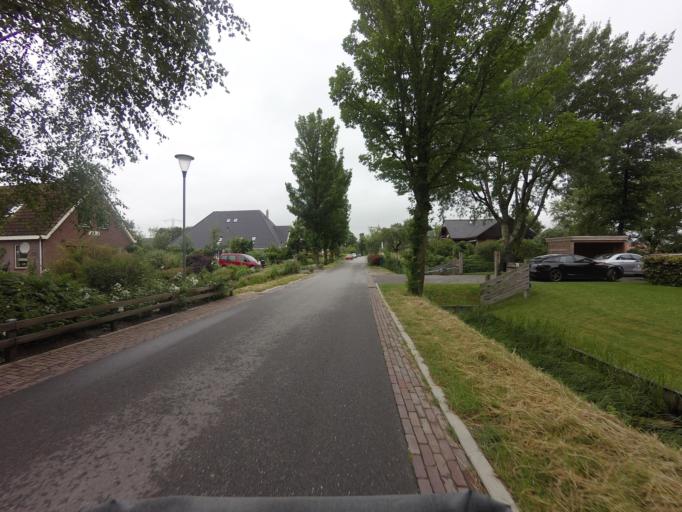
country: NL
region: North Holland
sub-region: Gemeente Schagen
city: Schagen
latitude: 52.7723
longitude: 4.8288
